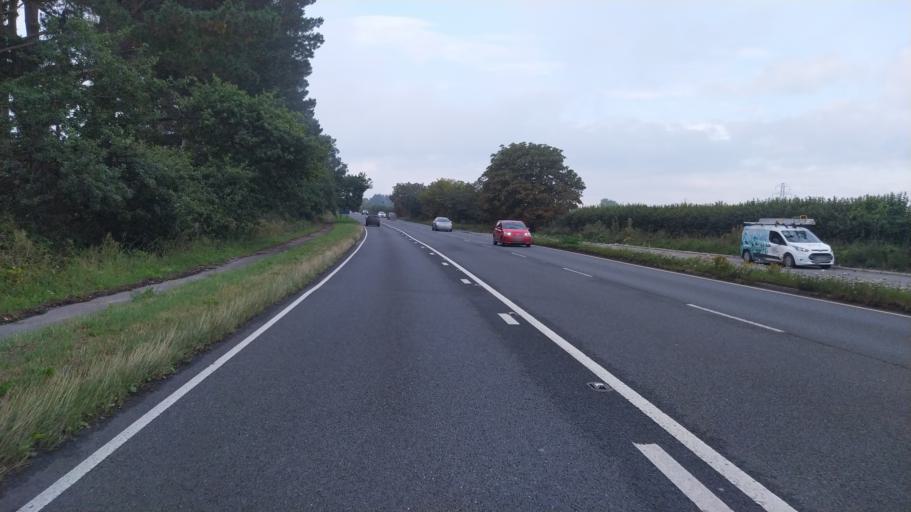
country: GB
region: England
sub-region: Hampshire
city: Bransgore
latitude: 50.7492
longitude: -1.7306
